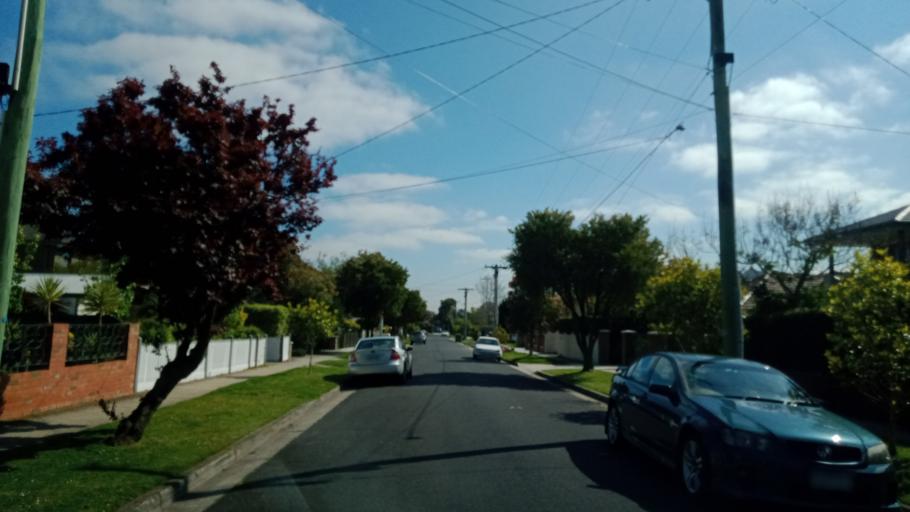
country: AU
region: Victoria
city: Hughesdale
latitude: -37.9142
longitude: 145.0760
